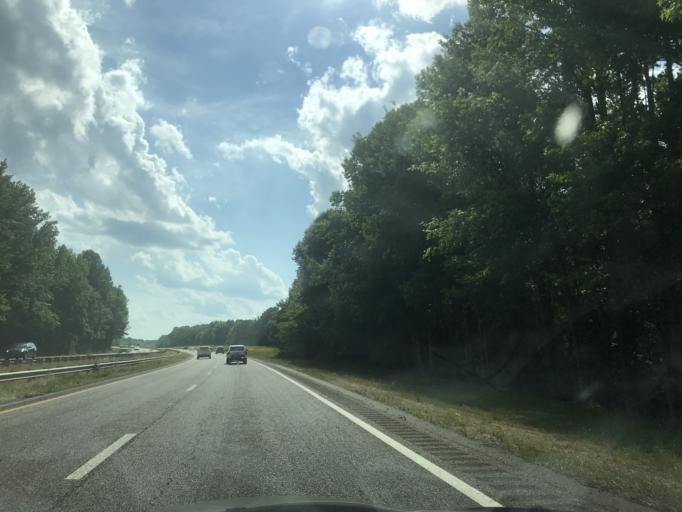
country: US
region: North Carolina
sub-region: Nash County
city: Nashville
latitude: 35.9768
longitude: -77.9274
